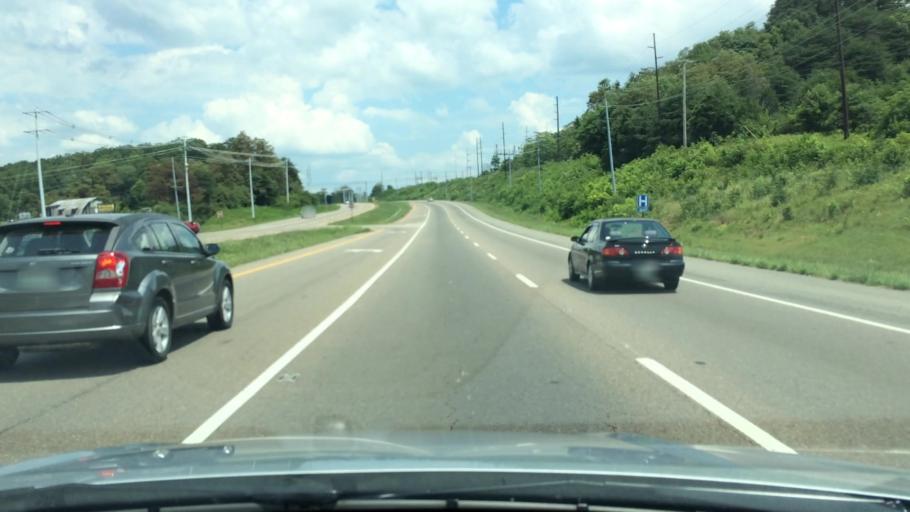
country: US
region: Tennessee
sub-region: Hamblen County
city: Morristown
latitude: 36.1876
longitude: -83.2970
